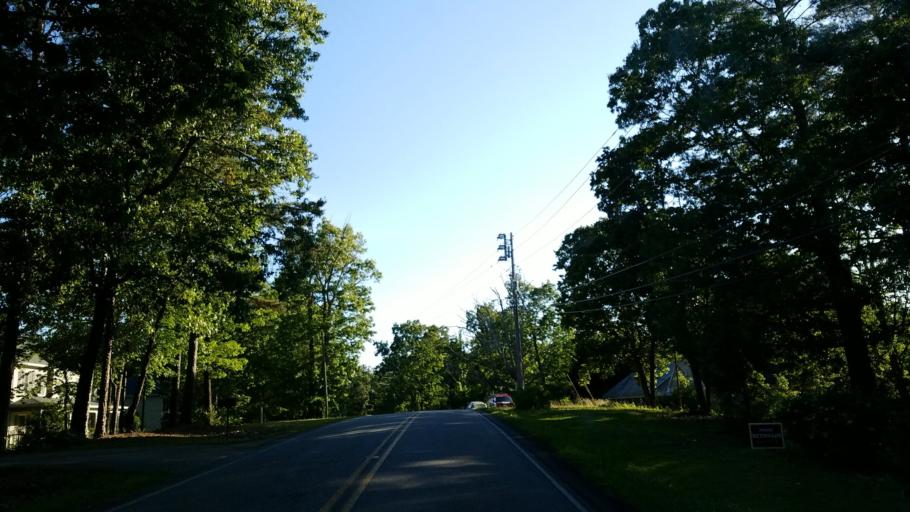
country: US
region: Georgia
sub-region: Cherokee County
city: Holly Springs
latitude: 34.1776
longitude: -84.5400
